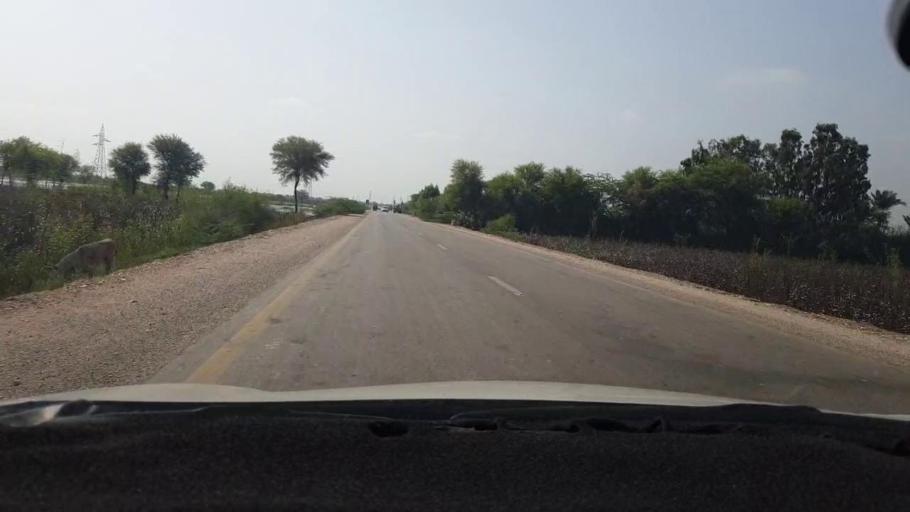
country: PK
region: Sindh
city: Tando Mittha Khan
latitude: 25.8201
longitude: 69.0659
